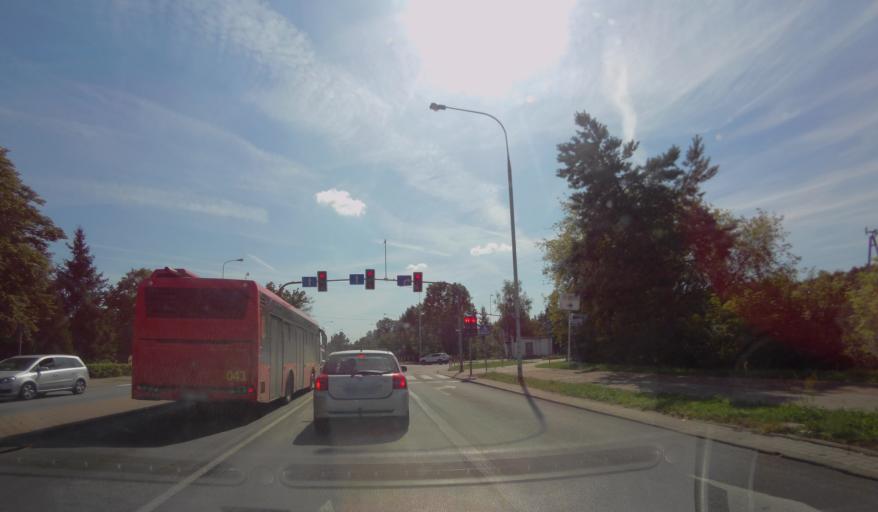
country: PL
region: Subcarpathian Voivodeship
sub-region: Powiat stalowowolski
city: Stalowa Wola
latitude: 50.5485
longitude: 22.0769
